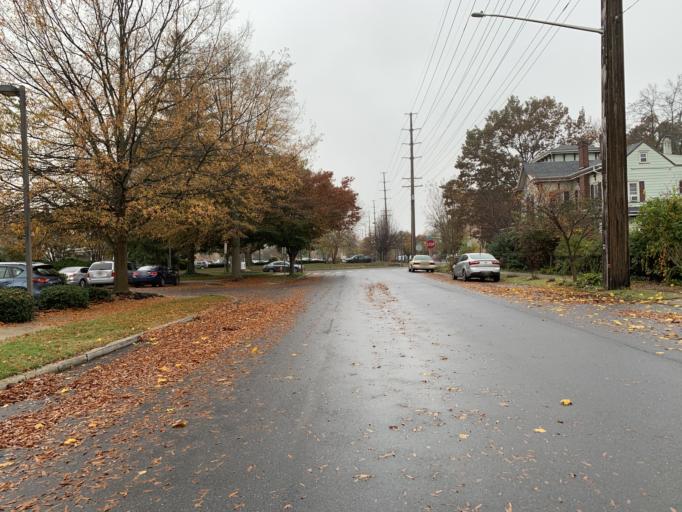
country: US
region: Delaware
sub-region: Kent County
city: Dover
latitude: 39.1631
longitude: -75.5256
